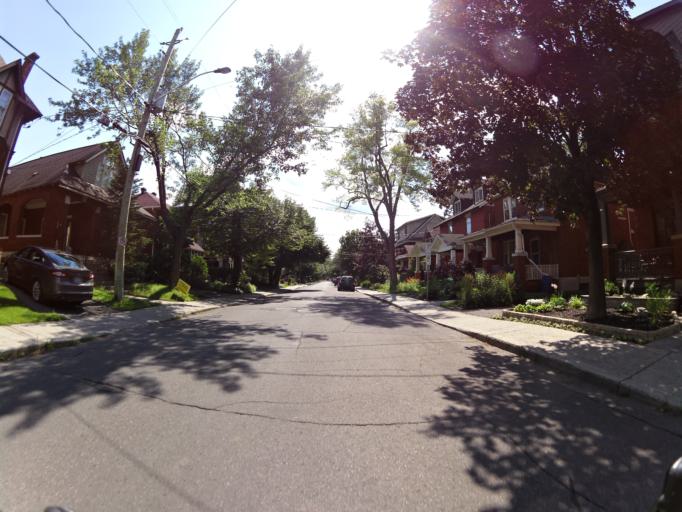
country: CA
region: Ontario
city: Ottawa
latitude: 45.3906
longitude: -75.6846
